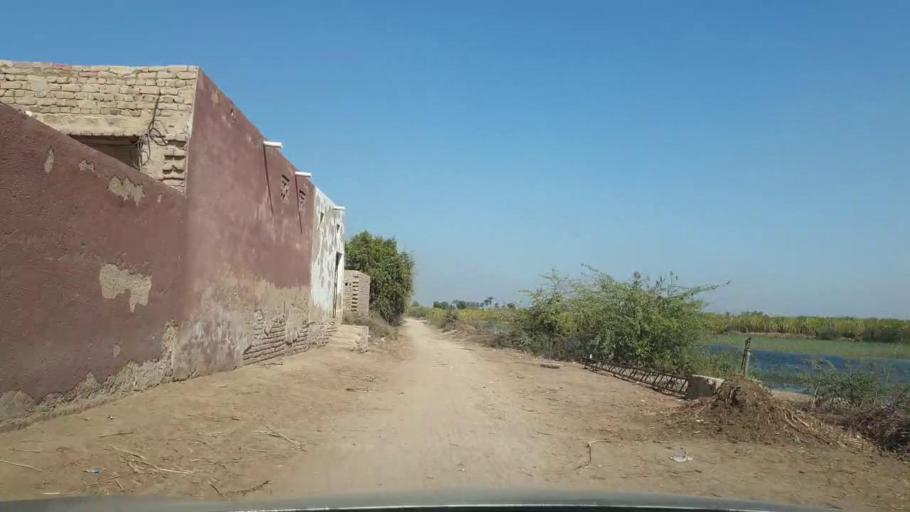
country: PK
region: Sindh
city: Tando Adam
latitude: 25.6319
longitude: 68.6671
